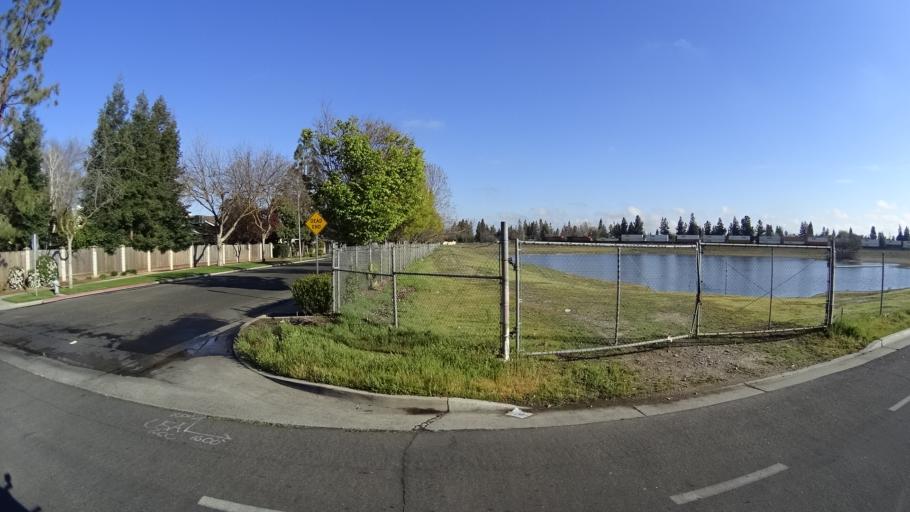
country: US
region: California
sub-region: Fresno County
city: West Park
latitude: 36.8153
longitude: -119.8578
